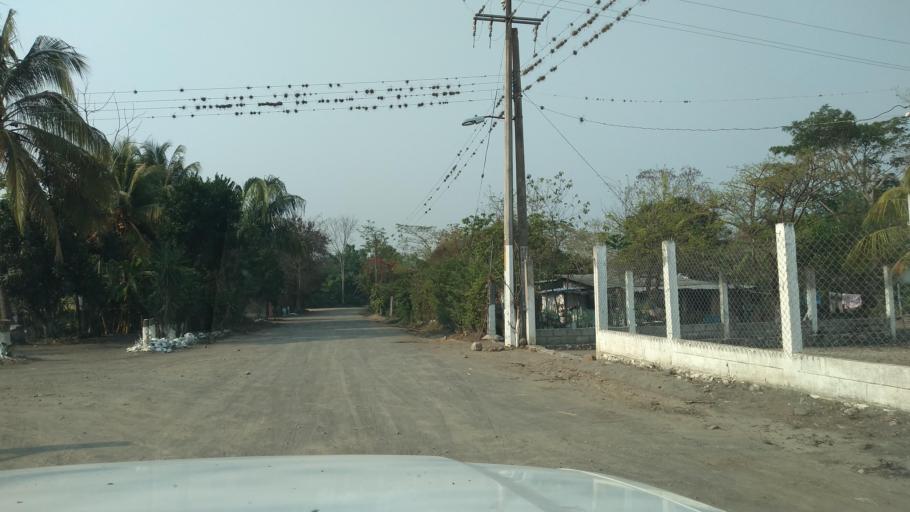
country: MX
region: Oaxaca
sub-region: Cosolapa
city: Cosolapa
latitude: 18.6234
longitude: -96.6074
